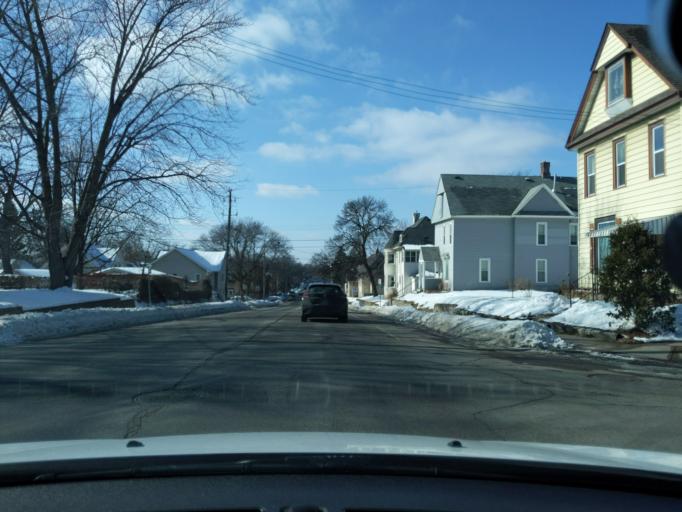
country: US
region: Minnesota
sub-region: Hennepin County
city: Saint Anthony
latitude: 45.0132
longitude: -93.2410
